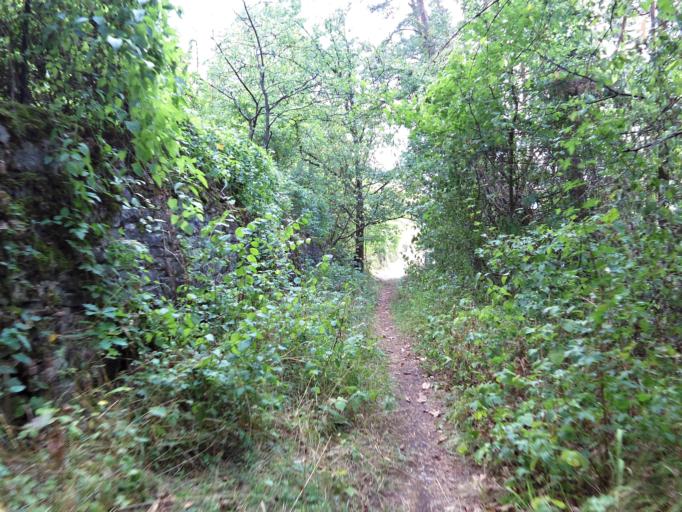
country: DE
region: Bavaria
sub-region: Regierungsbezirk Unterfranken
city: Margetshochheim
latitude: 49.8454
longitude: 9.8753
